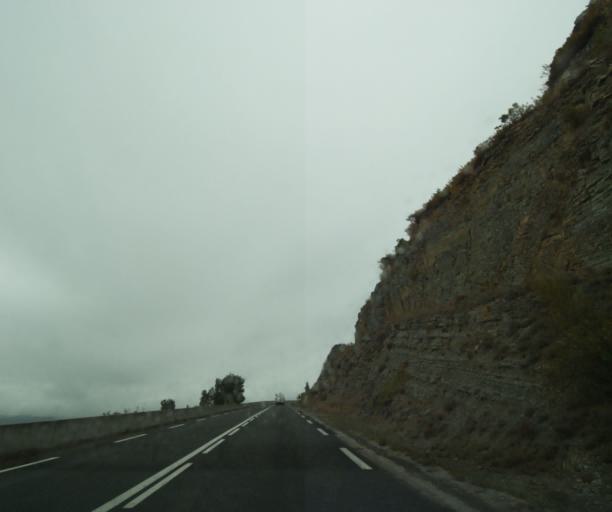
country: FR
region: Midi-Pyrenees
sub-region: Departement de l'Aveyron
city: Millau
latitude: 44.0887
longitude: 3.1017
